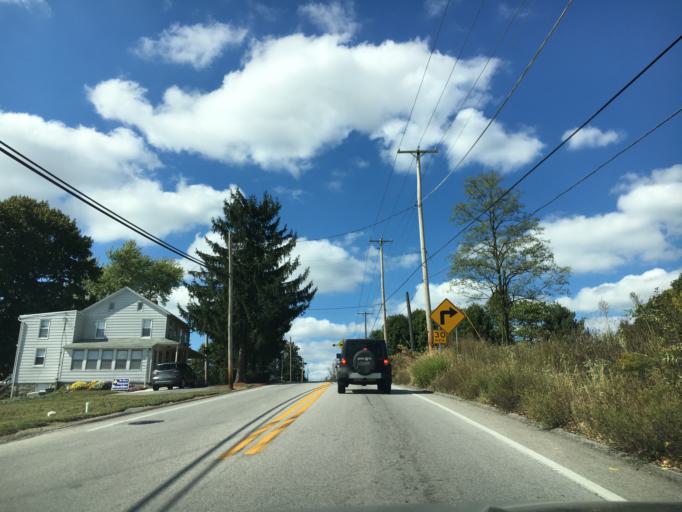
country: US
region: Pennsylvania
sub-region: York County
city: East York
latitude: 40.0006
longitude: -76.6809
